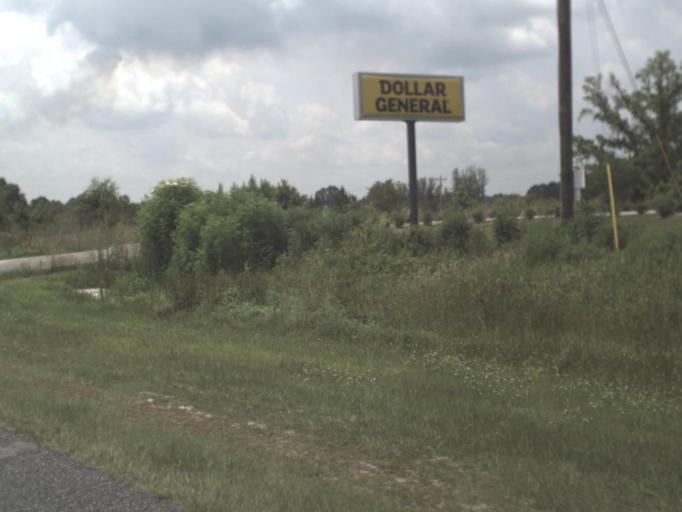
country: US
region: Florida
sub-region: Putnam County
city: East Palatka
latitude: 29.7735
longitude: -81.6394
